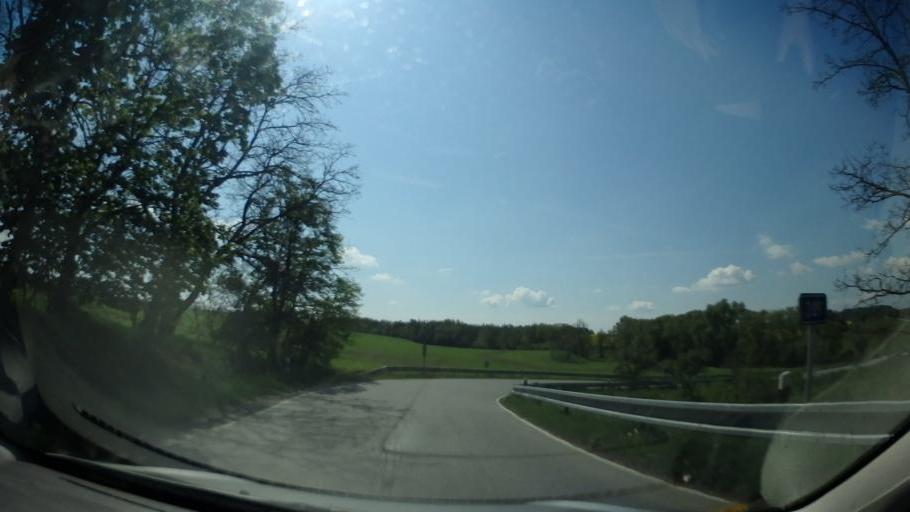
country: CZ
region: Vysocina
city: Namest' nad Oslavou
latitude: 49.2037
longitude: 16.0993
